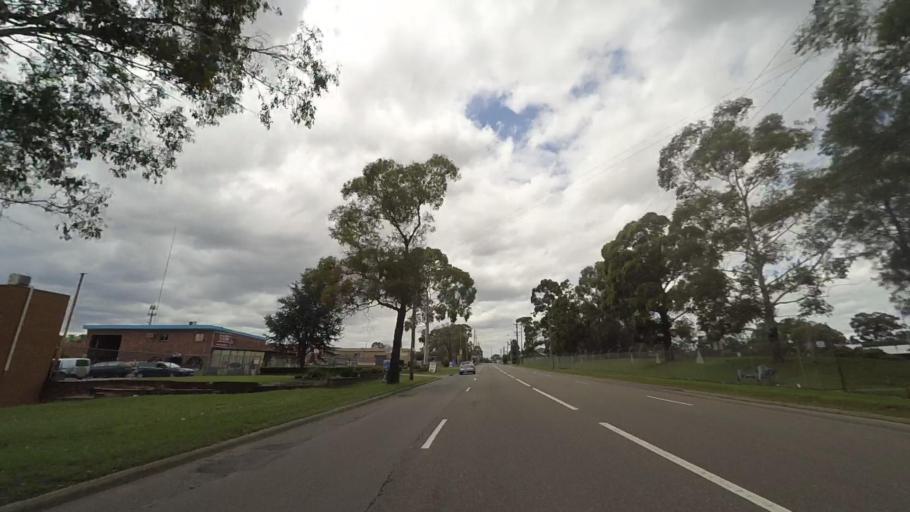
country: AU
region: New South Wales
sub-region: Holroyd
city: Guildford West
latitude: -33.8549
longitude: 150.9595
